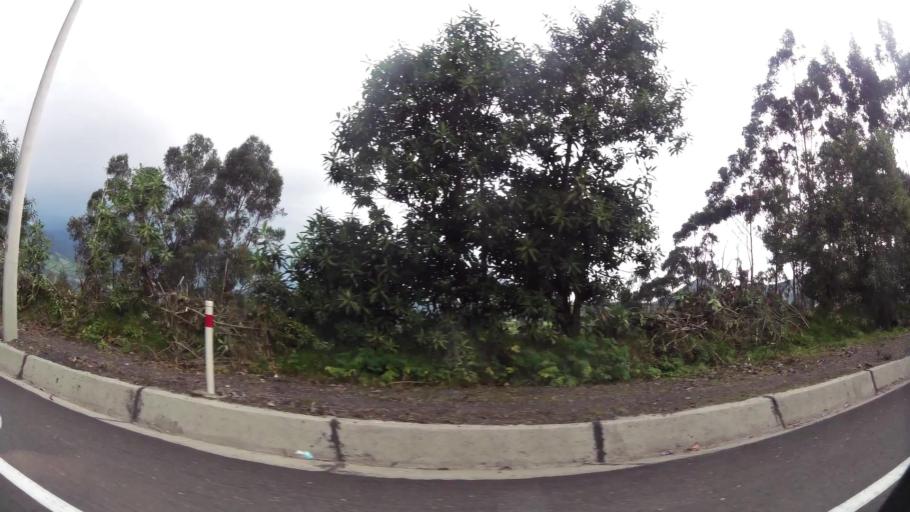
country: EC
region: Pichincha
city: Sangolqui
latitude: -0.3889
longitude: -78.5488
